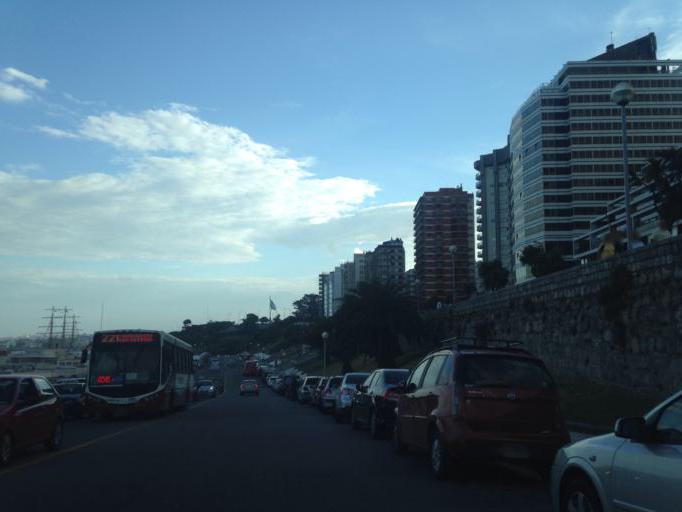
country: AR
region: Buenos Aires
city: Mar del Plata
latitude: -38.0268
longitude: -57.5325
